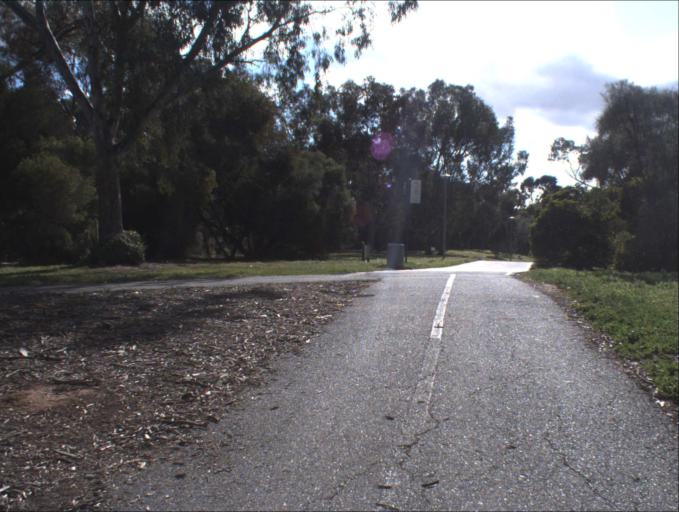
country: AU
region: South Australia
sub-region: Port Adelaide Enfield
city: Klemzig
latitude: -34.8871
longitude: 138.6345
